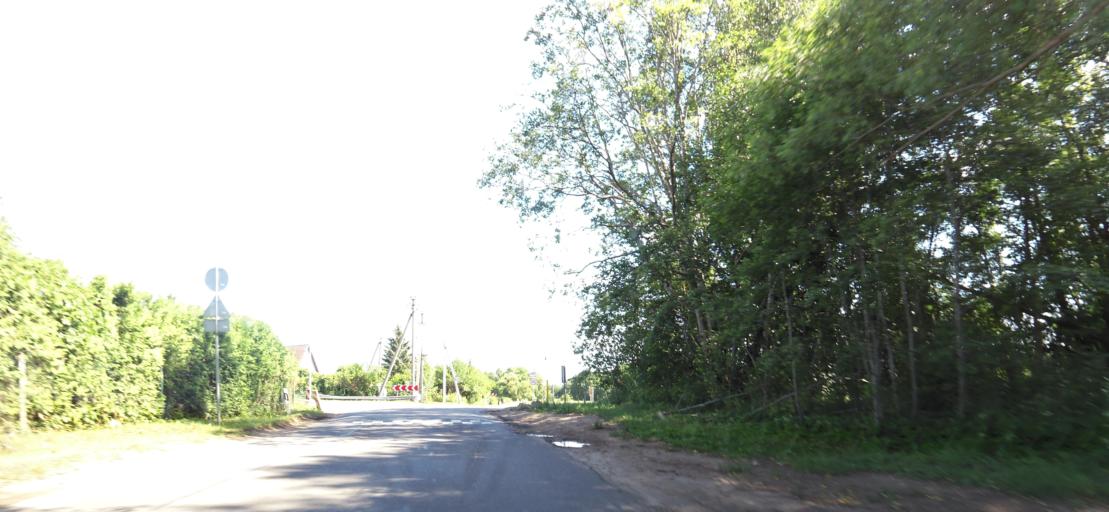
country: LT
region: Vilnius County
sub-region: Vilnius
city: Fabijoniskes
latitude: 54.8003
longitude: 25.3329
